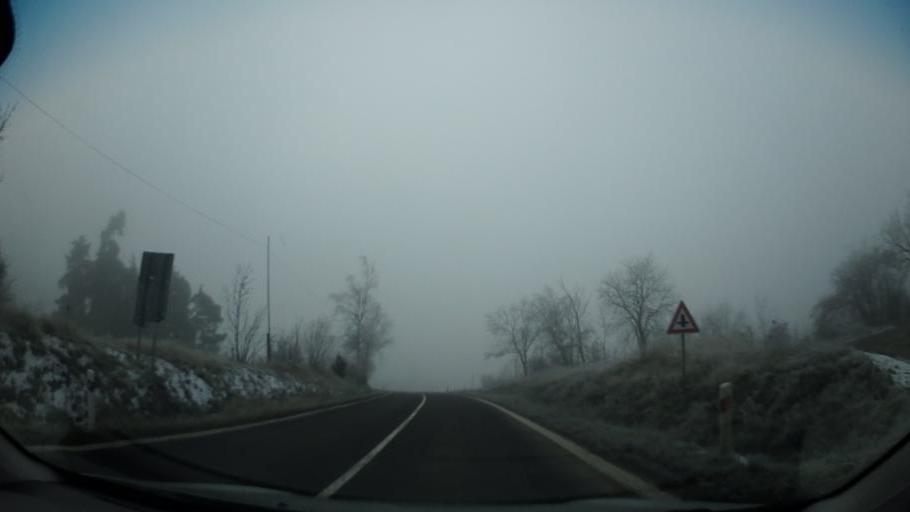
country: CZ
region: Vysocina
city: Budisov
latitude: 49.2806
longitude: 15.9456
